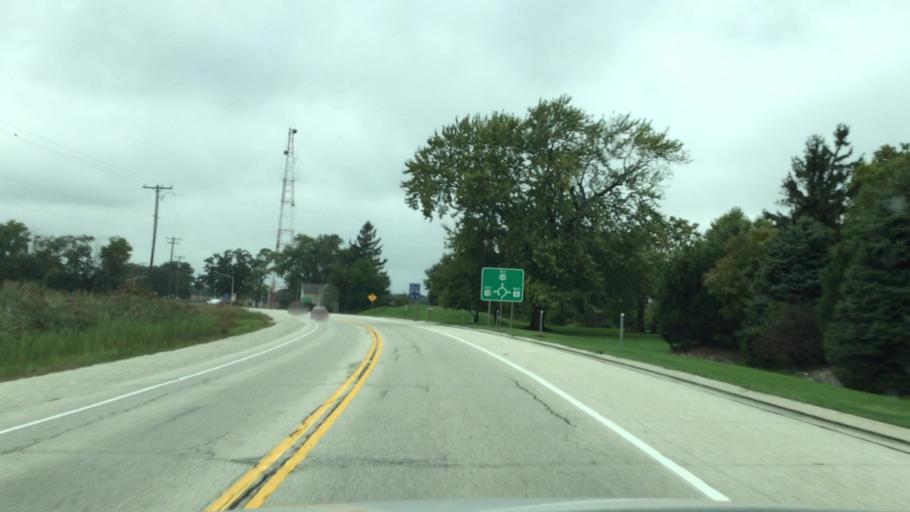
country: US
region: Wisconsin
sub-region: Racine County
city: Eagle Lake
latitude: 42.7418
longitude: -88.1063
